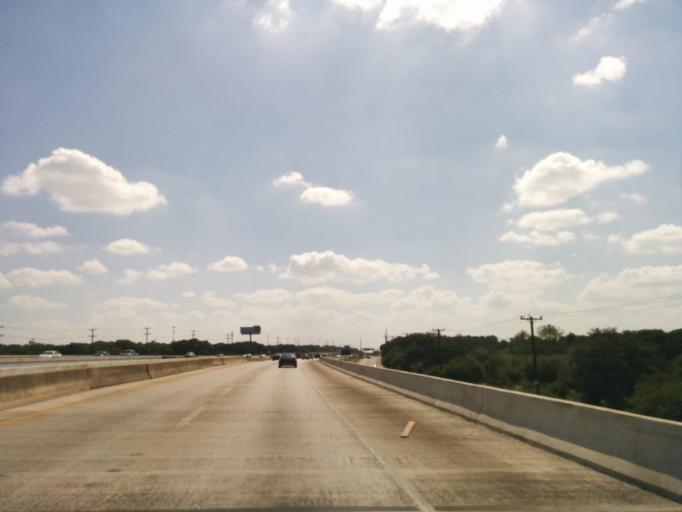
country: US
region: Texas
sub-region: Bexar County
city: Shavano Park
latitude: 29.5940
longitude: -98.5766
